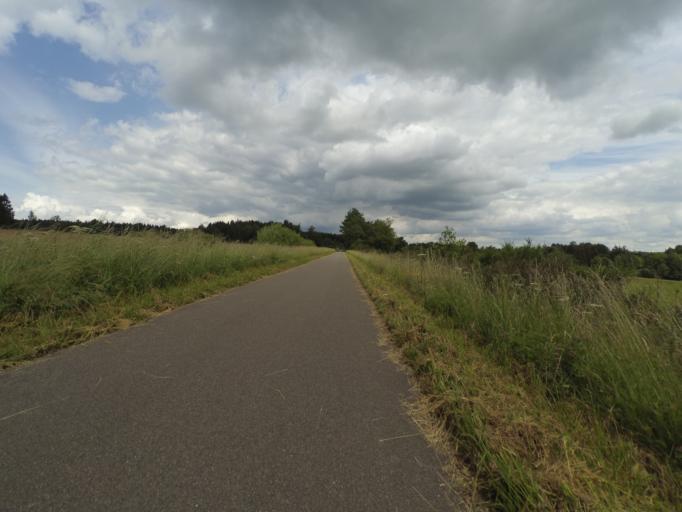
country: DE
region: North Rhine-Westphalia
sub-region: Regierungsbezirk Koln
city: Monschau
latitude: 50.5882
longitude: 6.2414
